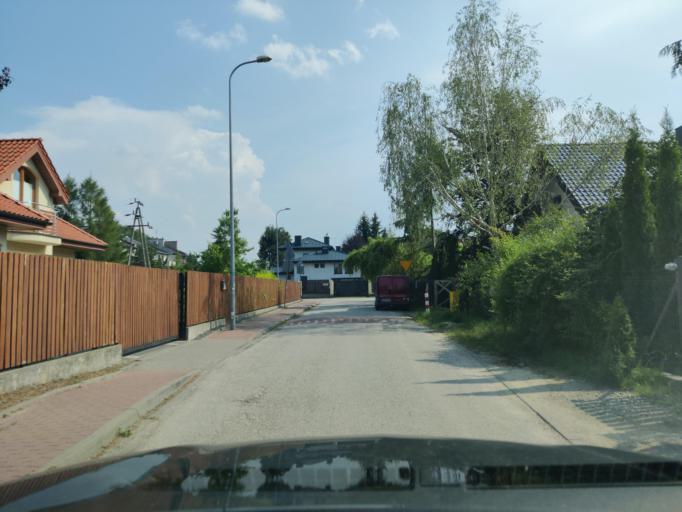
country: PL
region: Masovian Voivodeship
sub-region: Powiat pruszkowski
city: Nadarzyn
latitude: 52.1033
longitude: 20.7953
